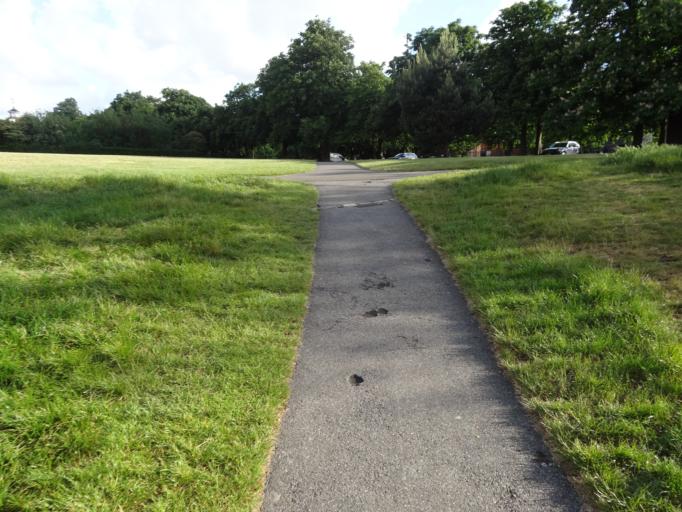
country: GB
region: England
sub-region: Greater London
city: Blackheath
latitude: 51.4778
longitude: 0.0001
